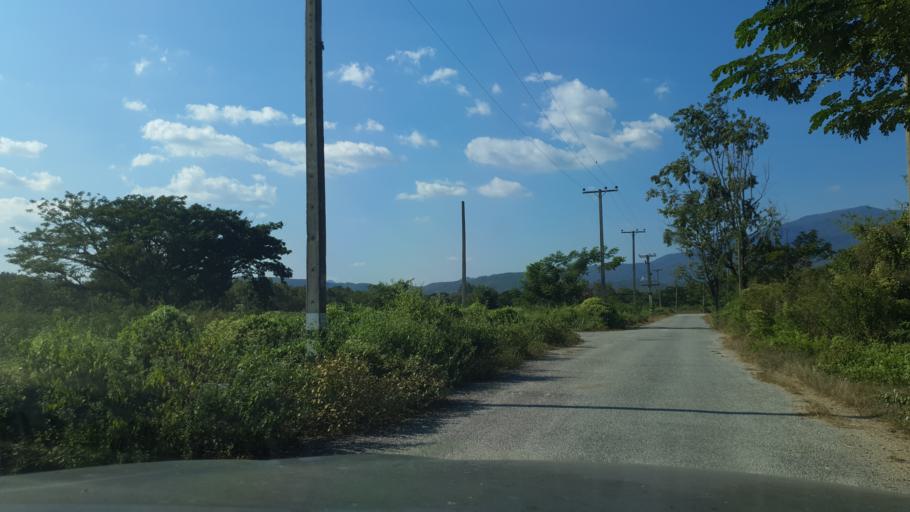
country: TH
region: Chiang Mai
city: Hang Dong
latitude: 18.7354
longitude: 98.9445
